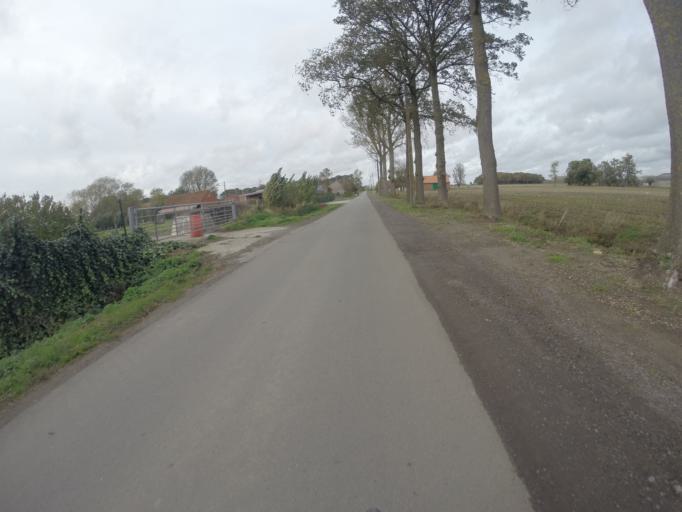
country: BE
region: Flanders
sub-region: Provincie Oost-Vlaanderen
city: Knesselare
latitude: 51.1566
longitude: 3.4030
